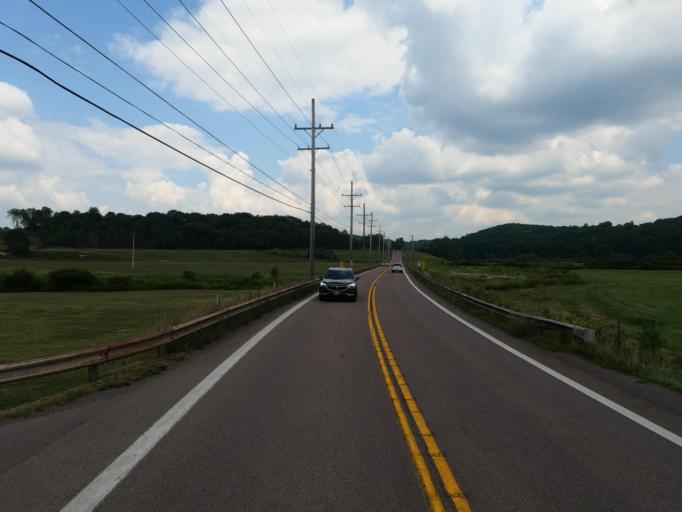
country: US
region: Pennsylvania
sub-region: Somerset County
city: Meyersdale
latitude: 39.6795
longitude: -79.1718
